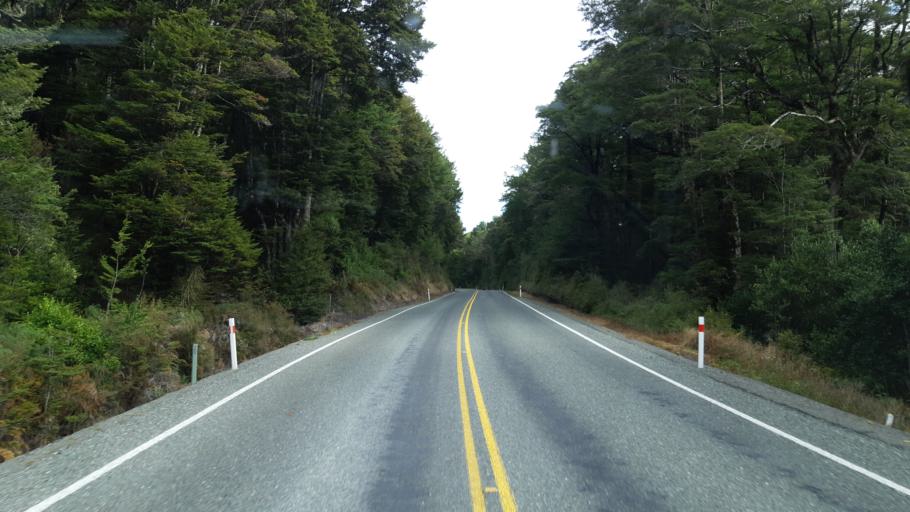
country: NZ
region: Tasman
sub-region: Tasman District
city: Wakefield
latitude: -41.7798
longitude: 172.9101
